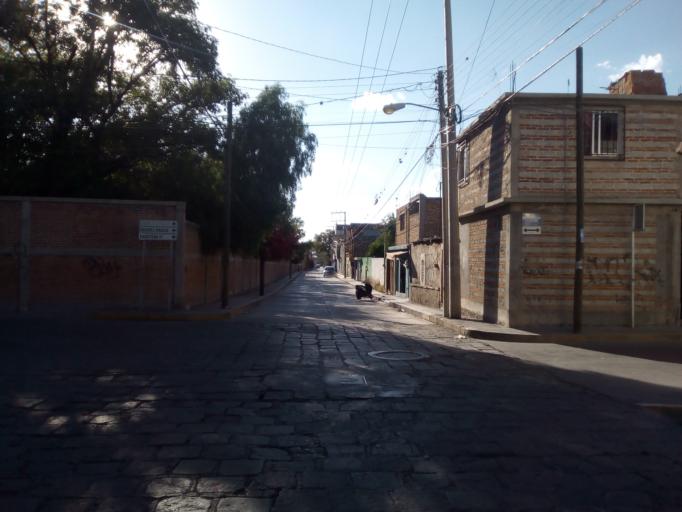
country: MX
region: Guanajuato
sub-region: San Luis de la Paz
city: San Luis de la Paz
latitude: 21.3018
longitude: -100.5219
